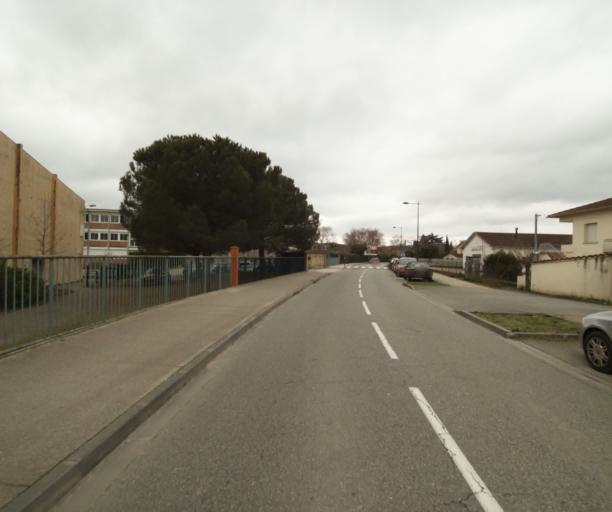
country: FR
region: Midi-Pyrenees
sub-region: Departement de l'Ariege
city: Pamiers
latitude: 43.1170
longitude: 1.6220
